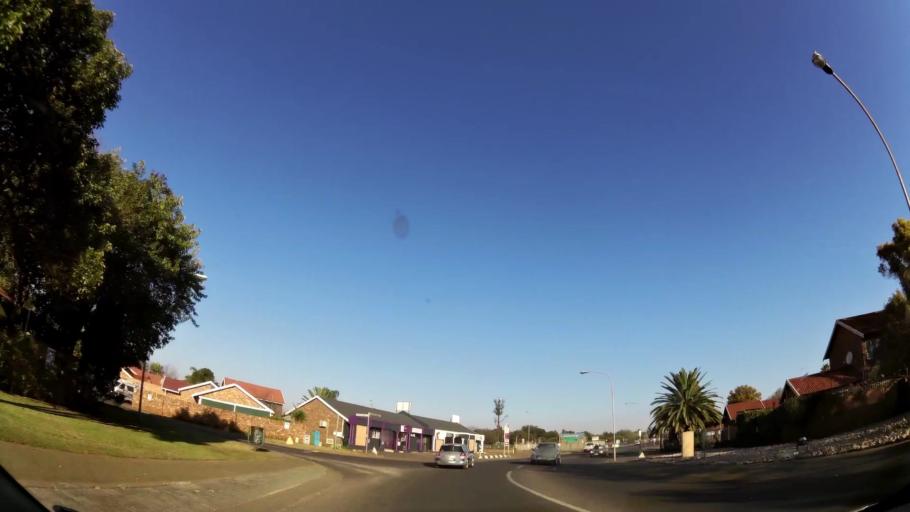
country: ZA
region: Gauteng
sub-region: City of Tshwane Metropolitan Municipality
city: Centurion
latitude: -25.8671
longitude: 28.1515
